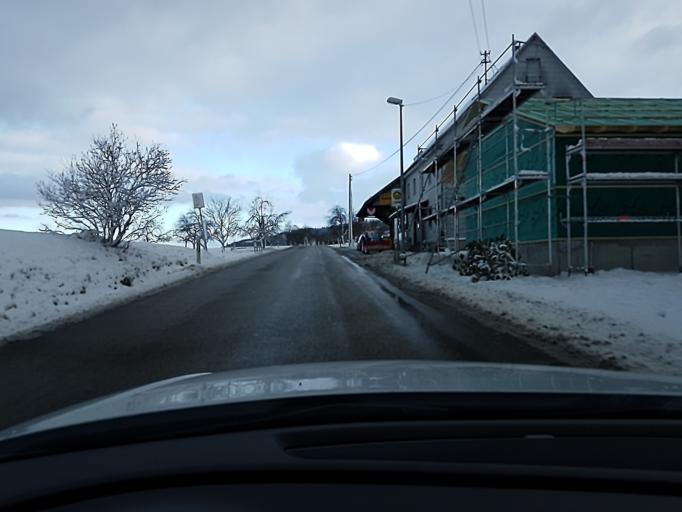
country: DE
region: Baden-Wuerttemberg
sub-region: Regierungsbezirk Stuttgart
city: Kaisersbach
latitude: 48.9528
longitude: 9.6736
